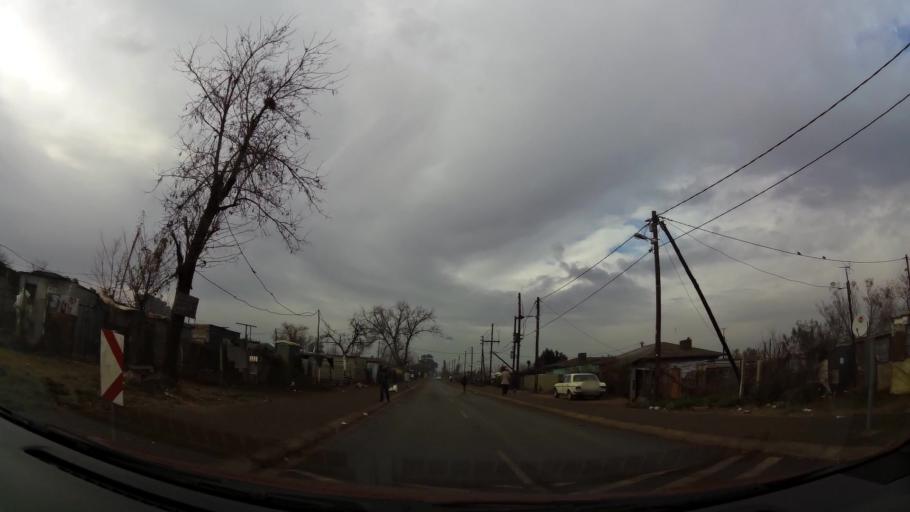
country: ZA
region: Gauteng
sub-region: City of Johannesburg Metropolitan Municipality
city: Soweto
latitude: -26.2845
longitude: 27.8375
